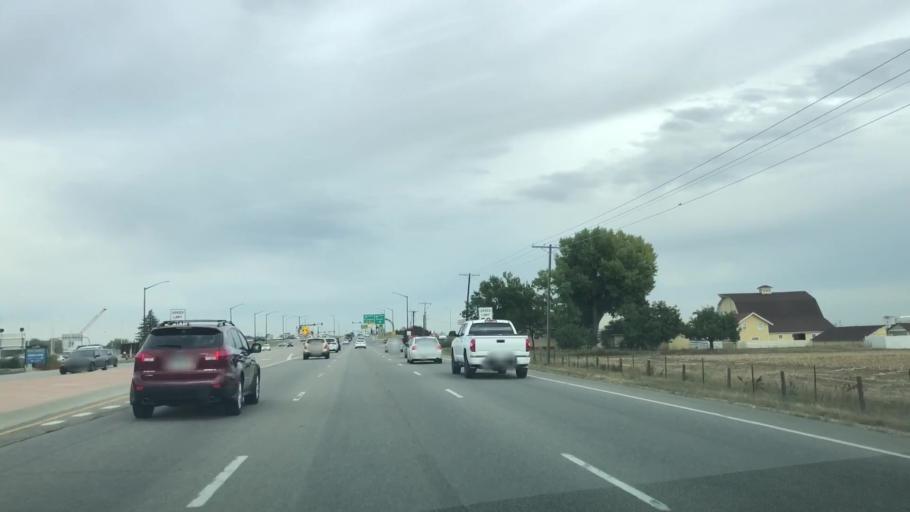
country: US
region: Colorado
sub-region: Larimer County
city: Loveland
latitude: 40.4070
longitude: -104.9996
